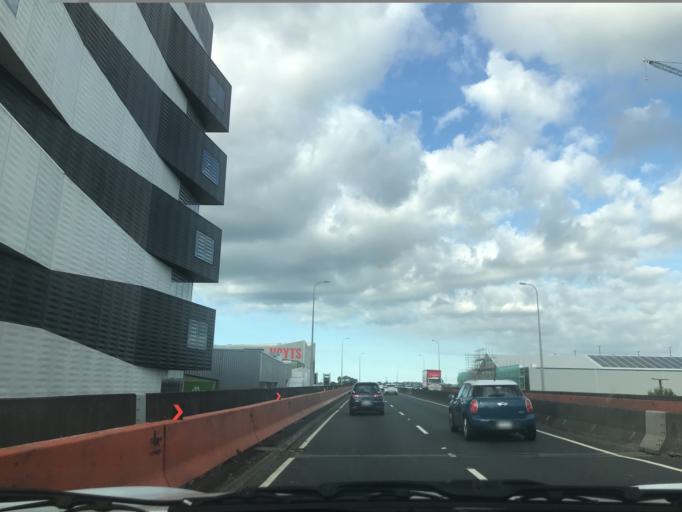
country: NZ
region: Auckland
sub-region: Auckland
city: Tamaki
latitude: -36.9155
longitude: 174.8400
